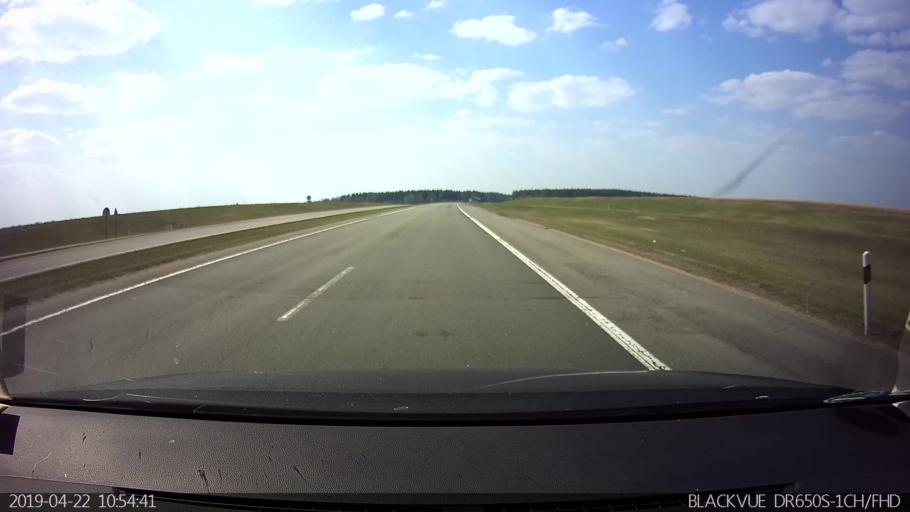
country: BY
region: Minsk
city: Krupki
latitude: 54.3357
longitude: 29.1019
